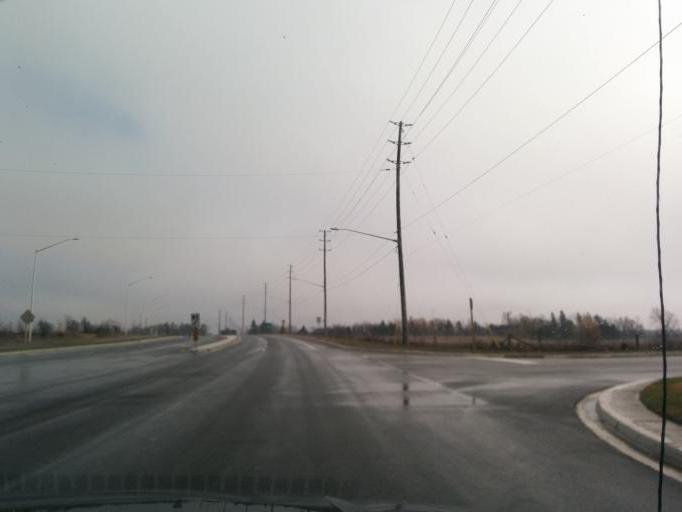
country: CA
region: Ontario
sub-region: Halton
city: Milton
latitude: 43.4977
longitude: -79.9011
